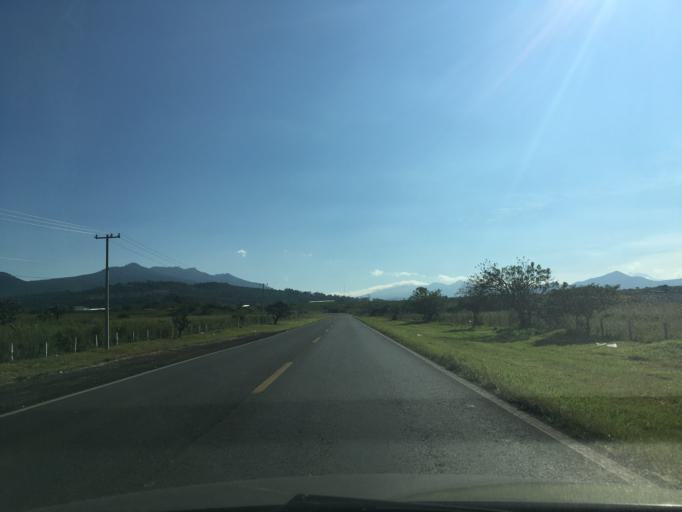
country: MX
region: Mexico
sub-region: Chalco
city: Los Nogales
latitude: 19.8549
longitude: -102.1413
